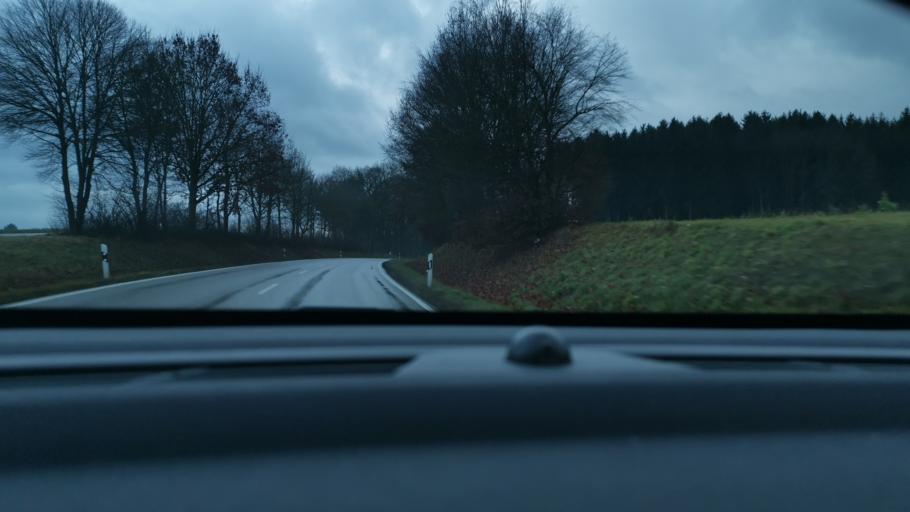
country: DE
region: Bavaria
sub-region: Swabia
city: Petersdorf
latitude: 48.4983
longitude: 11.0156
